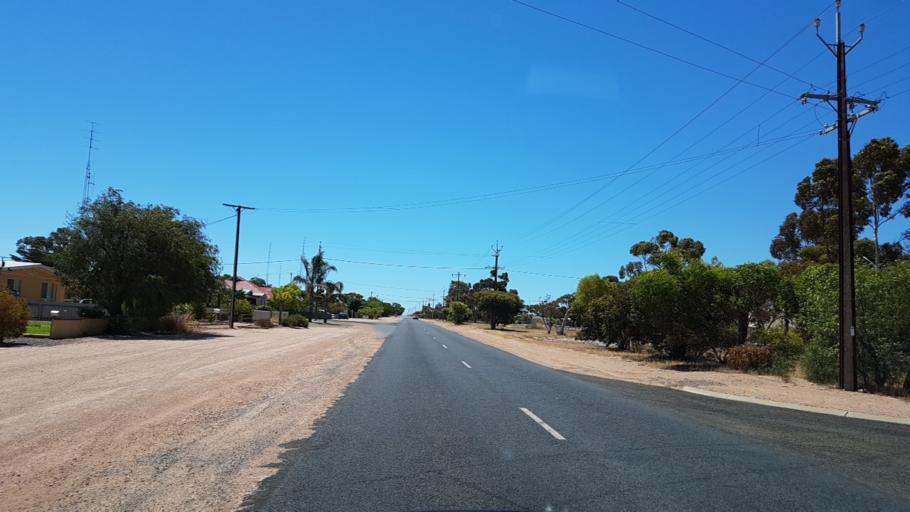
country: AU
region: South Australia
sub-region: Copper Coast
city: Wallaroo
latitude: -34.0569
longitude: 137.5930
